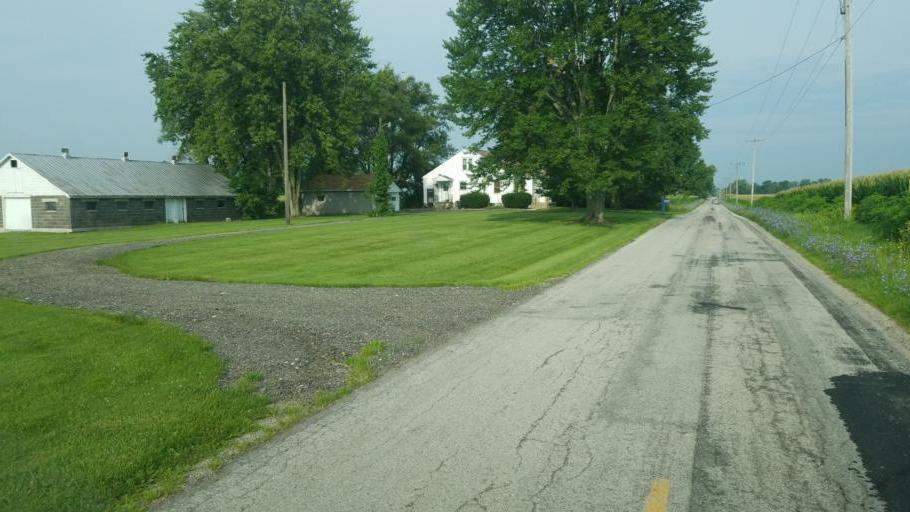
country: US
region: Ohio
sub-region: Delaware County
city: Ashley
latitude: 40.4733
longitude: -83.0295
